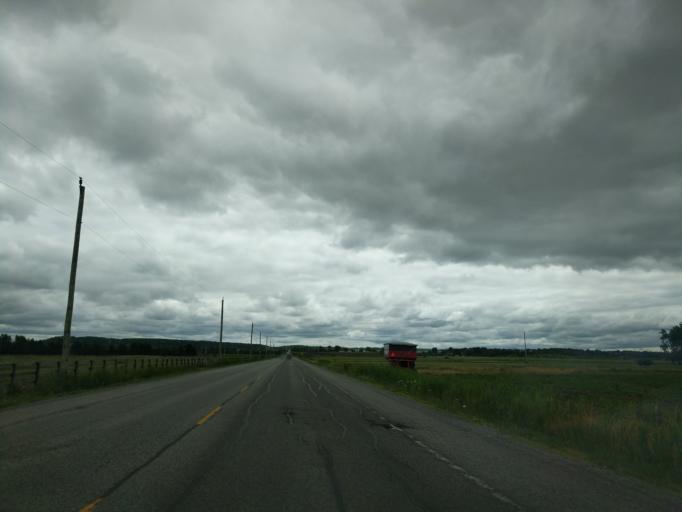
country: CA
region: Ontario
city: Thorold
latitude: 43.1757
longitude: -79.1689
